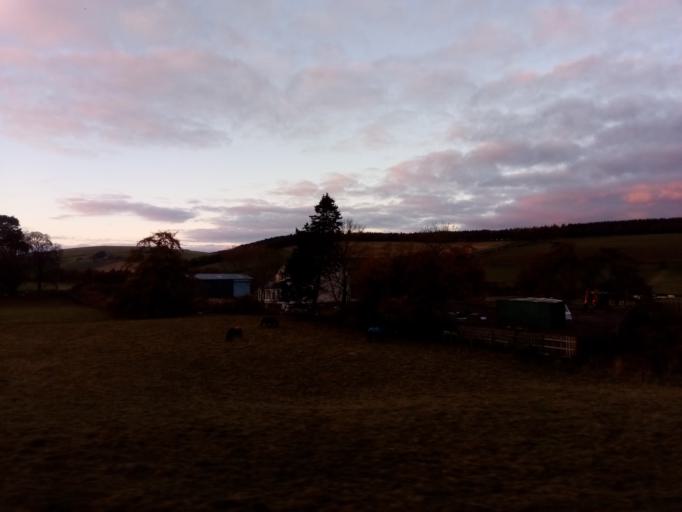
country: GB
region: Scotland
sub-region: The Scottish Borders
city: Lauder
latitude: 55.7725
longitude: -2.7997
